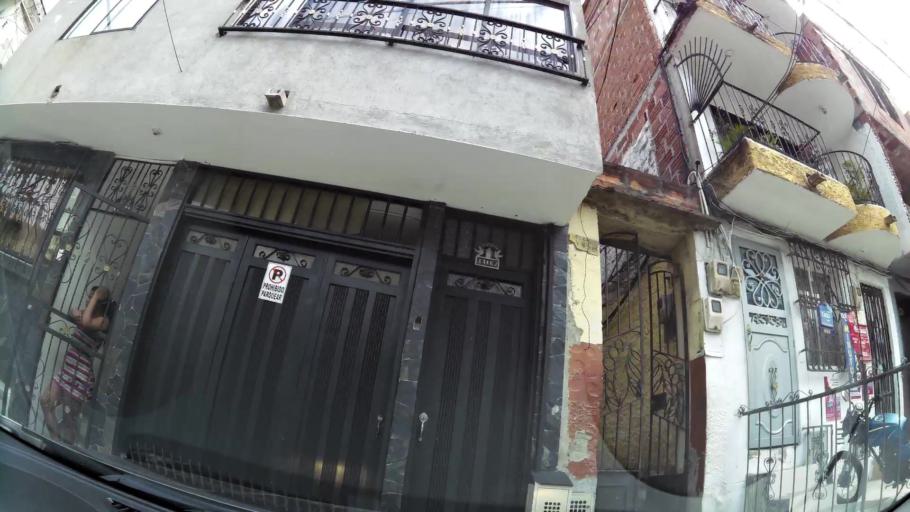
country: CO
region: Antioquia
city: Medellin
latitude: 6.2736
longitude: -75.5536
